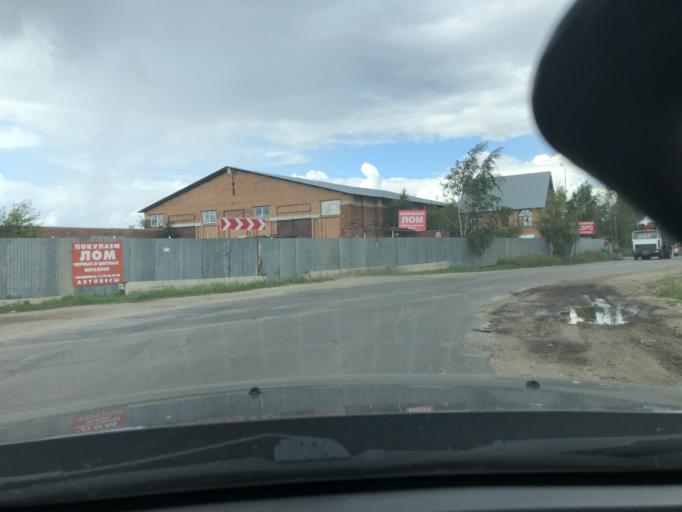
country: RU
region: Tula
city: Kamenetskiy
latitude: 54.0173
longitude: 38.2524
